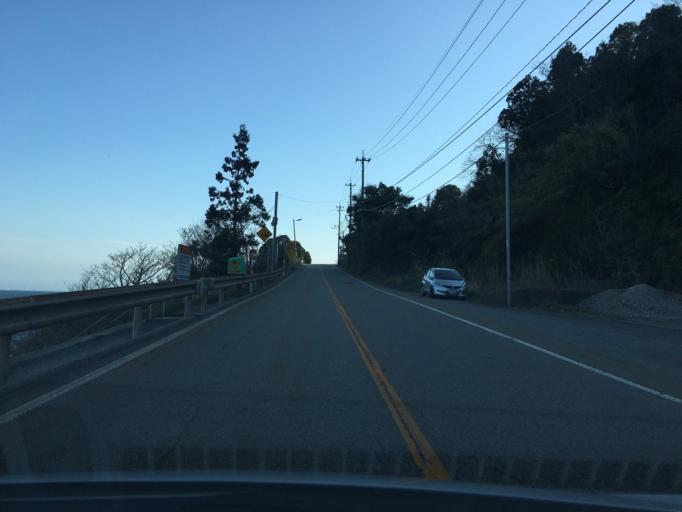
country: JP
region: Ishikawa
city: Nanao
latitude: 36.9934
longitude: 137.0530
